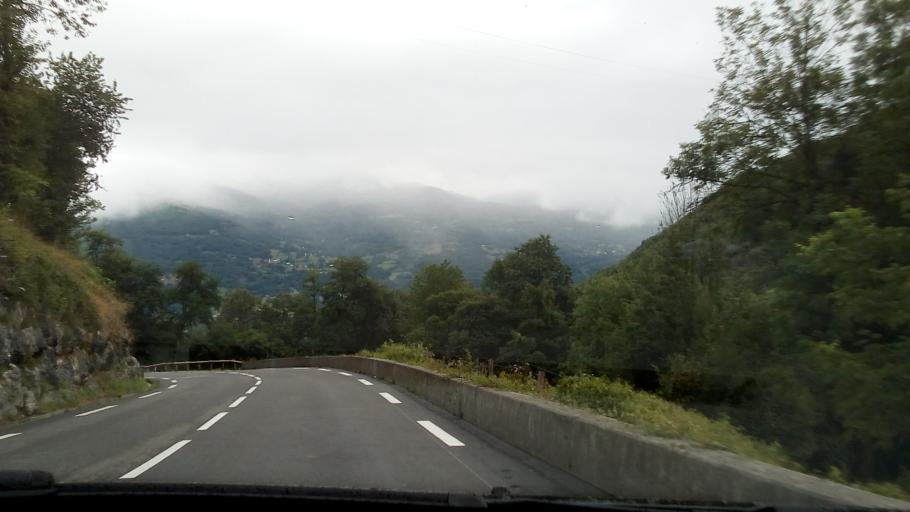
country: FR
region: Midi-Pyrenees
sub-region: Departement des Hautes-Pyrenees
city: Argeles-Gazost
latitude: 42.9987
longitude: -0.1139
